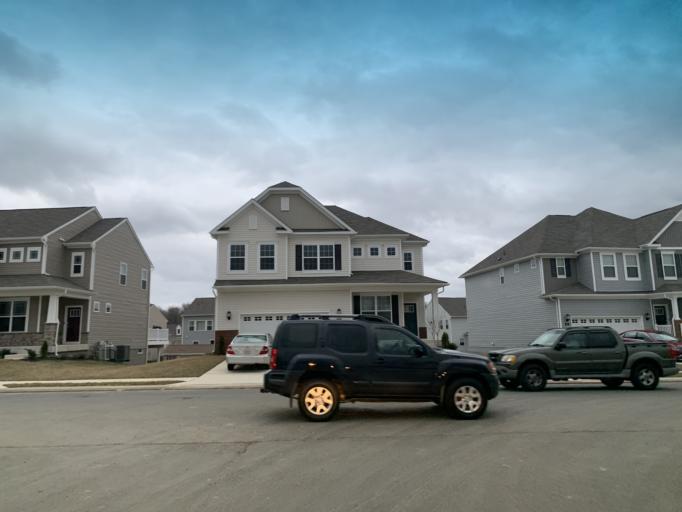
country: US
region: Maryland
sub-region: Harford County
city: Perryman
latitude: 39.4970
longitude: -76.2071
